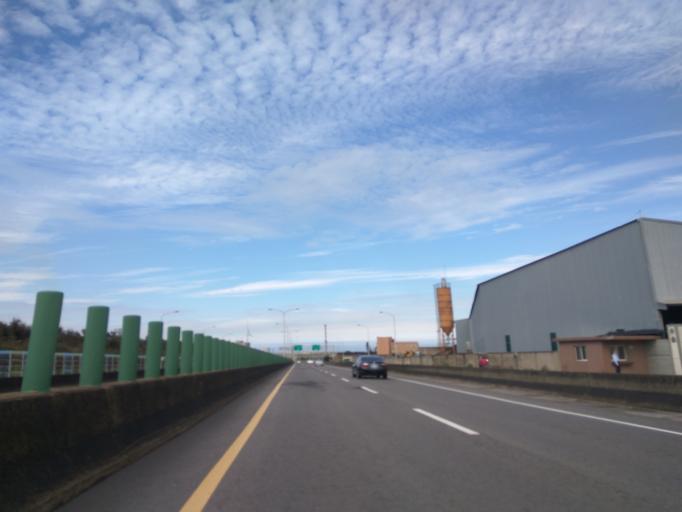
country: TW
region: Taiwan
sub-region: Hsinchu
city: Zhubei
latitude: 25.0270
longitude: 121.0585
